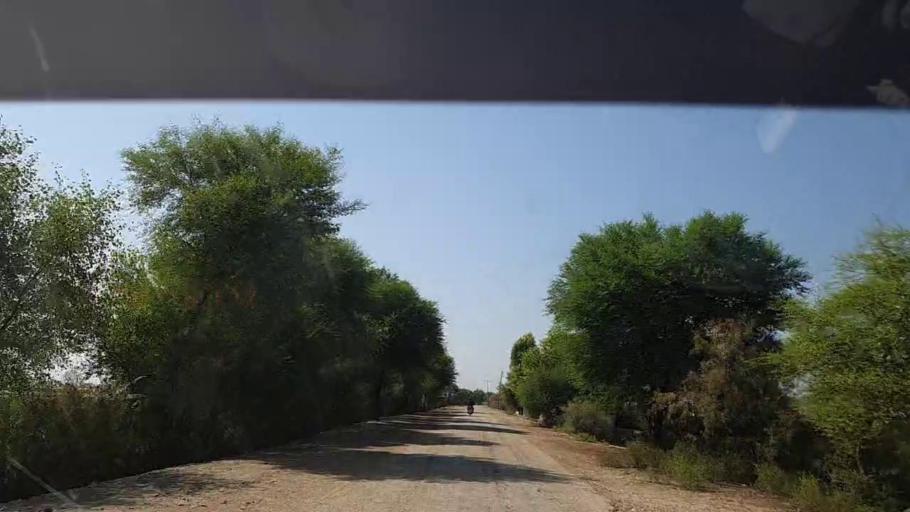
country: PK
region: Sindh
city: Ghauspur
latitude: 28.1961
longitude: 69.0475
